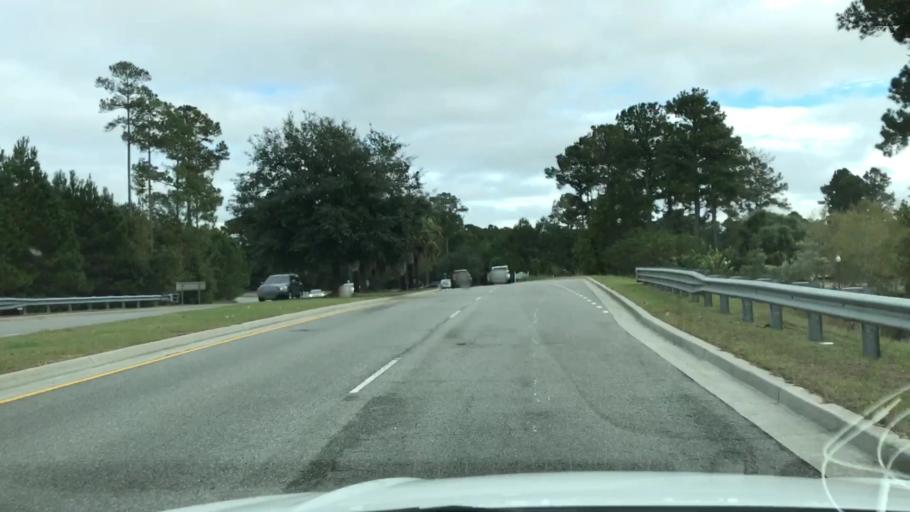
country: US
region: South Carolina
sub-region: Beaufort County
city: Bluffton
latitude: 32.2573
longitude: -80.8947
